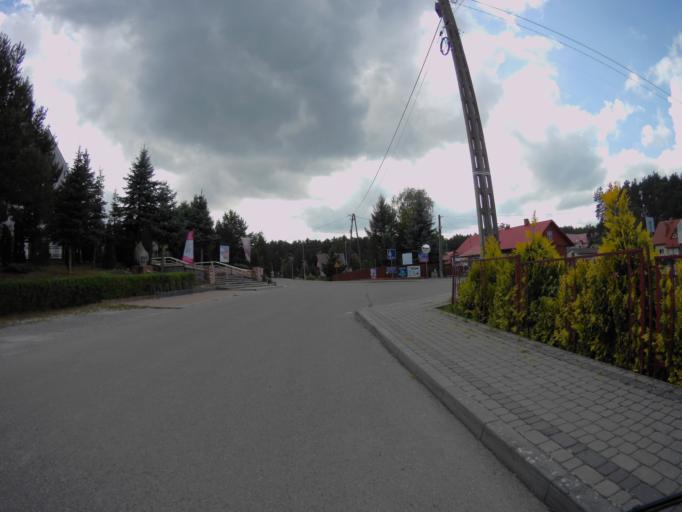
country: PL
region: Subcarpathian Voivodeship
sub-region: Powiat lezajski
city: Brzoza Krolewska
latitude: 50.2450
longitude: 22.3217
